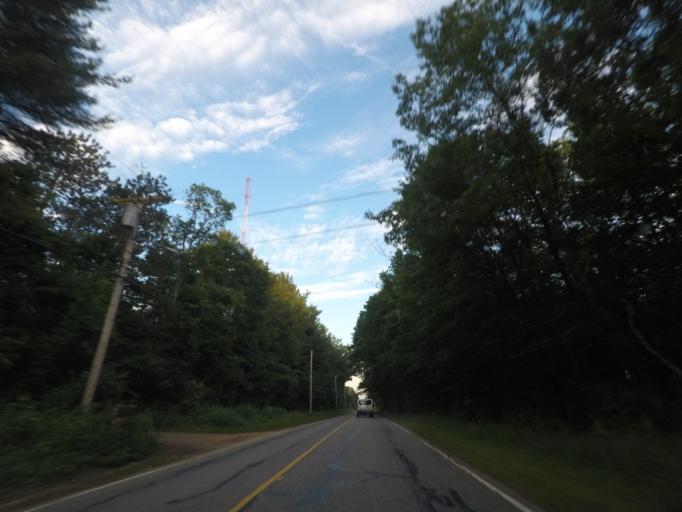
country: US
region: Massachusetts
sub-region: Worcester County
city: Warren
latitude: 42.1799
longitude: -72.1621
